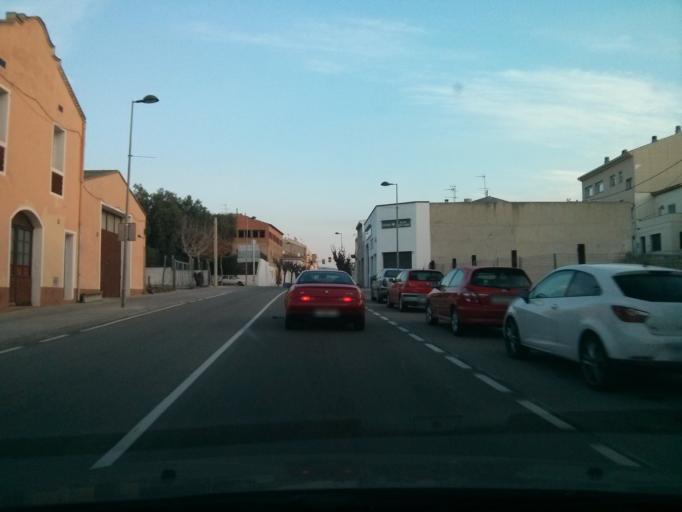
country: ES
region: Catalonia
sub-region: Provincia de Tarragona
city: Sant Jaume dels Domenys
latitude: 41.2810
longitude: 1.5535
